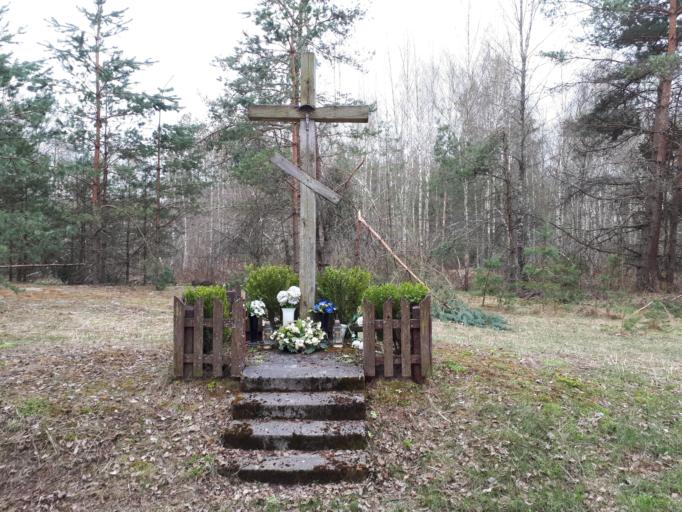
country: LT
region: Alytaus apskritis
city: Varena
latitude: 54.0097
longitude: 24.6381
